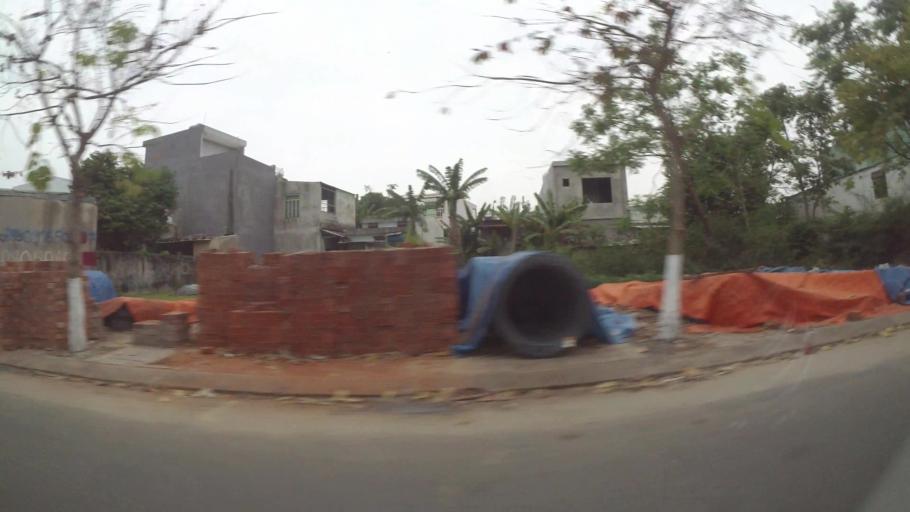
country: VN
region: Da Nang
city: Thanh Khe
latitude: 16.0505
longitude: 108.1762
